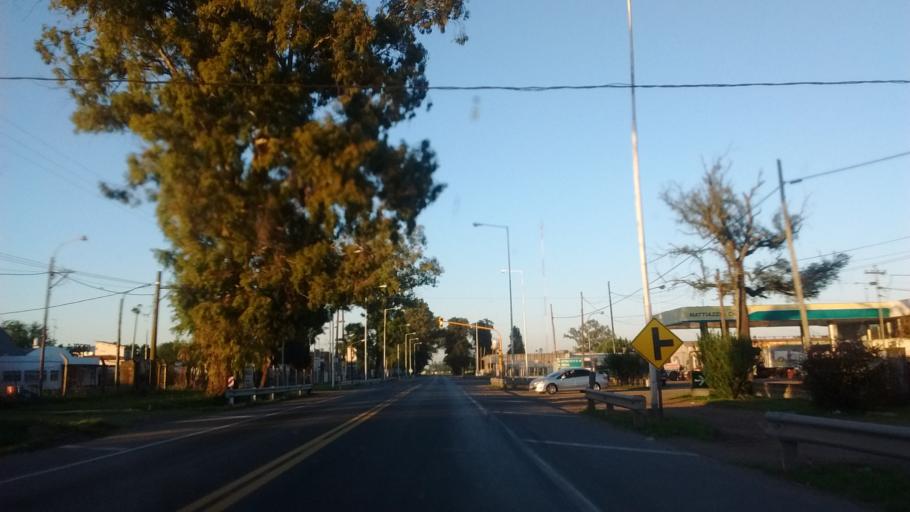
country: AR
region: Santa Fe
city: Casilda
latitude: -33.0681
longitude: -61.1845
